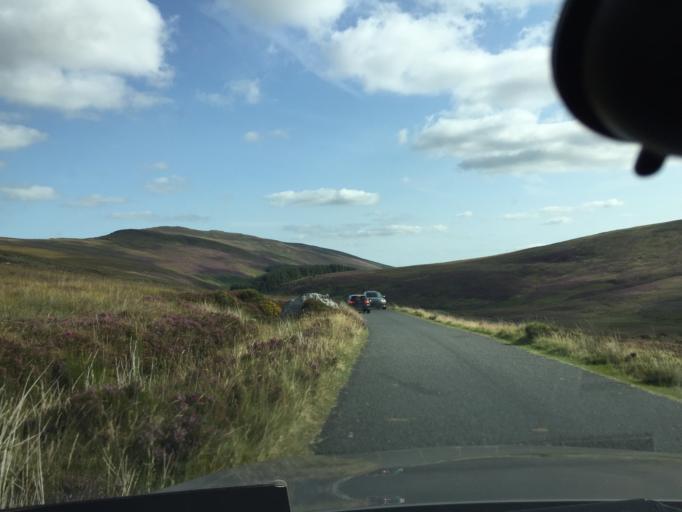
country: IE
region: Leinster
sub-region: Wicklow
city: Rathdrum
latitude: 53.0728
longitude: -6.3520
